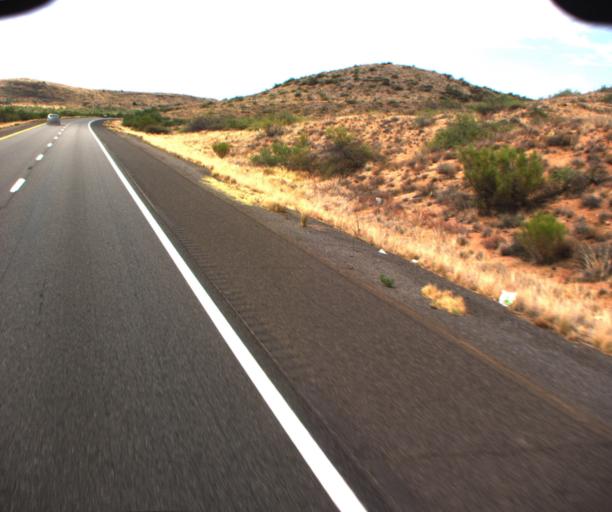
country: US
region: Arizona
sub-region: Yavapai County
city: Cordes Lakes
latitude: 34.2459
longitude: -112.1138
